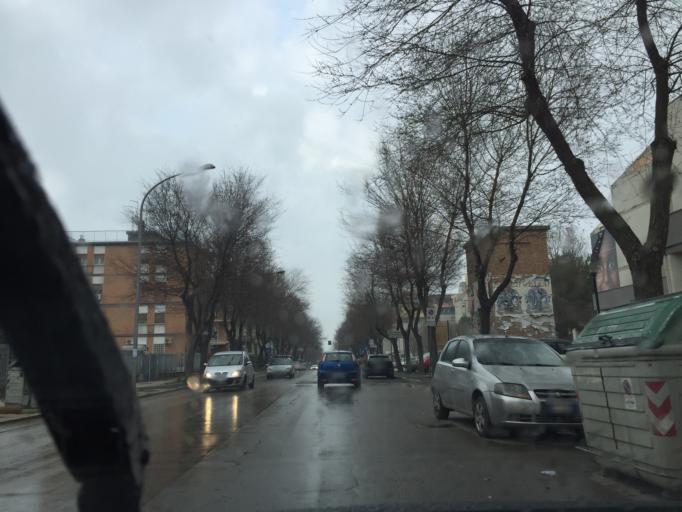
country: IT
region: Apulia
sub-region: Provincia di Foggia
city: Foggia
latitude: 41.4671
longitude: 15.5355
